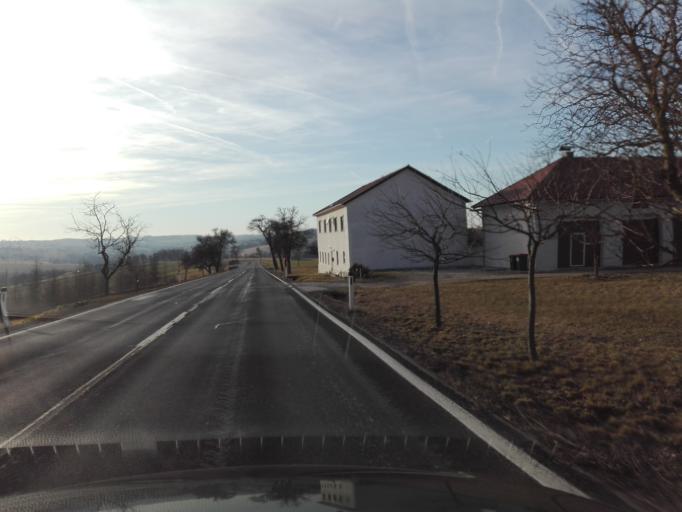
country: AT
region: Lower Austria
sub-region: Politischer Bezirk Amstetten
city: Strengberg
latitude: 48.1401
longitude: 14.6906
